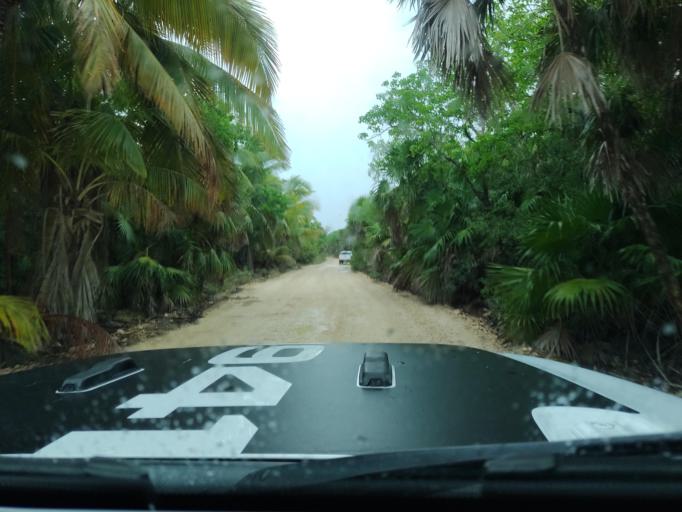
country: MX
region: Quintana Roo
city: Tulum
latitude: 20.0542
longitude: -87.4814
